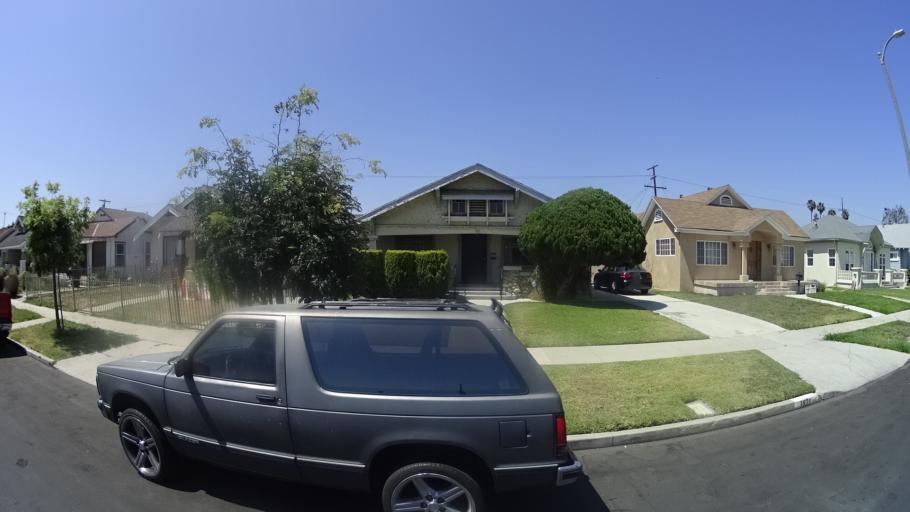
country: US
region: California
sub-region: Los Angeles County
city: View Park-Windsor Hills
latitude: 34.0081
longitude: -118.3120
